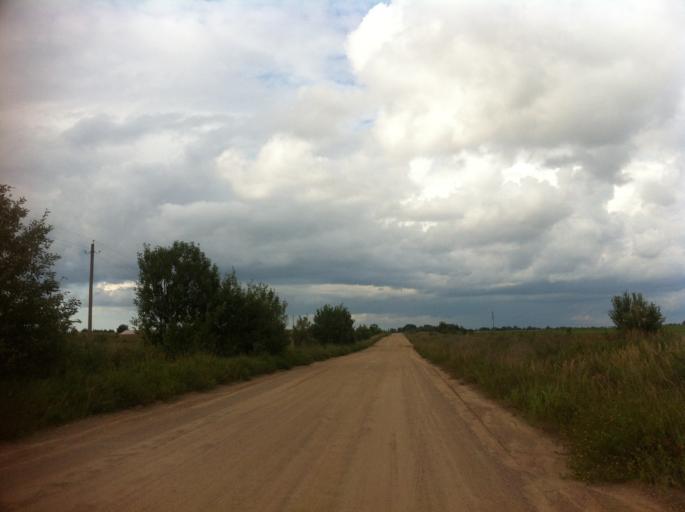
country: RU
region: Pskov
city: Izborsk
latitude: 57.8227
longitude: 27.9789
